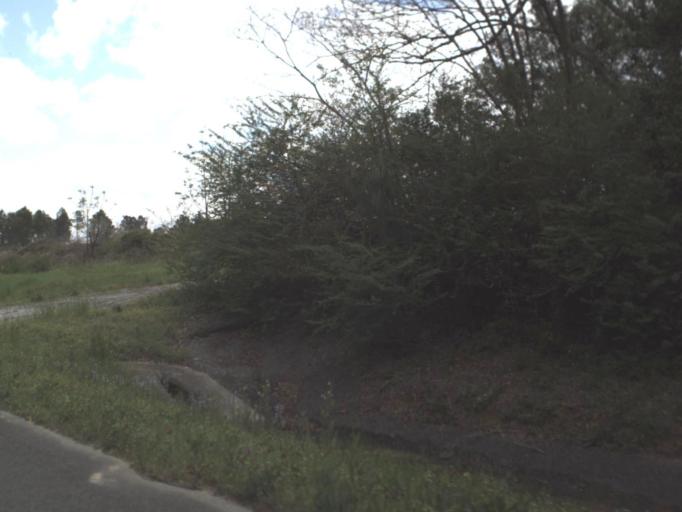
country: US
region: Florida
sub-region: Okaloosa County
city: Crestview
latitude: 30.8519
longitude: -86.6750
